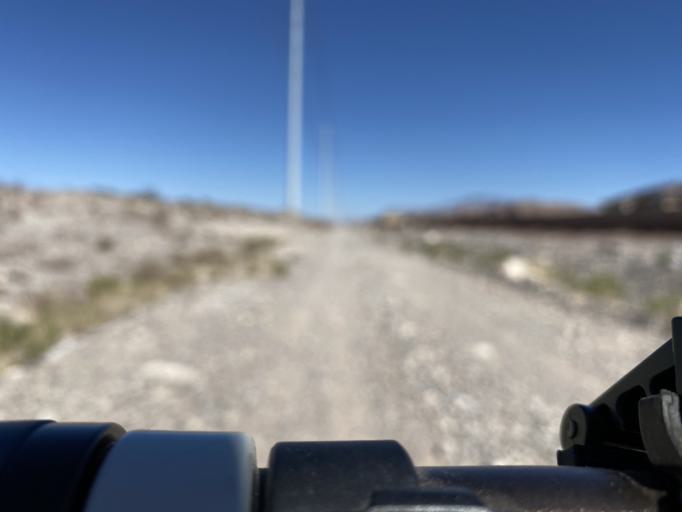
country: US
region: Nevada
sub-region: Clark County
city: Summerlin South
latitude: 36.2925
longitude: -115.3335
